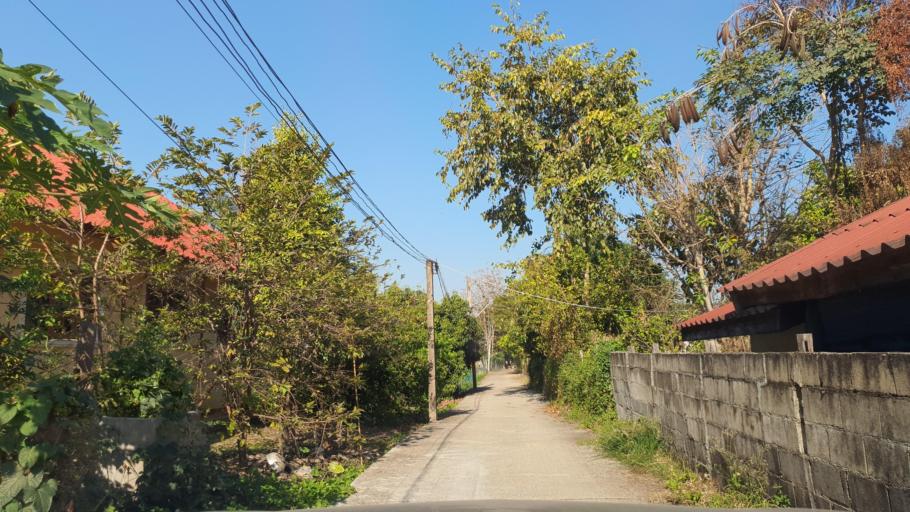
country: TH
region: Chiang Mai
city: San Kamphaeng
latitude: 18.7197
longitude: 99.1738
